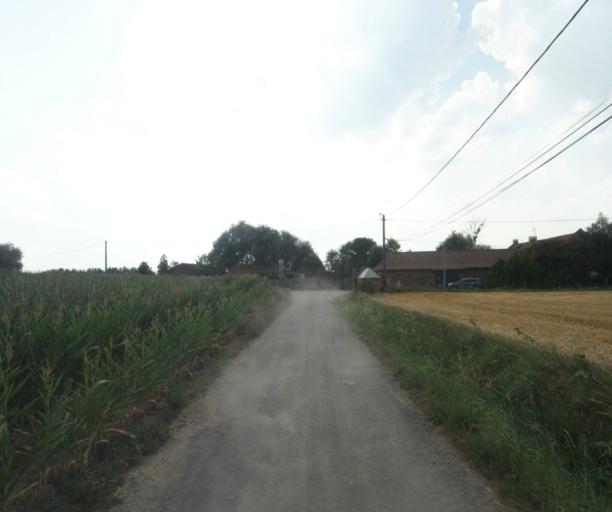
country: FR
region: Nord-Pas-de-Calais
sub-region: Departement du Nord
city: Linselles
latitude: 50.7256
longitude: 3.0605
